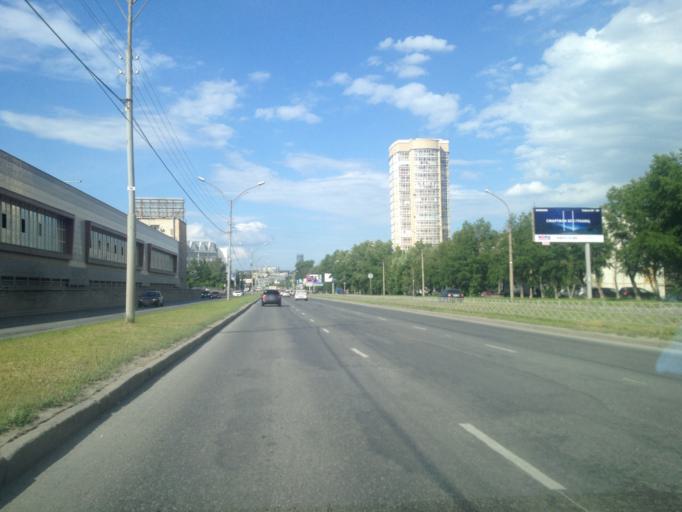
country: RU
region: Sverdlovsk
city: Sovkhoznyy
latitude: 56.8164
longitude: 60.5541
